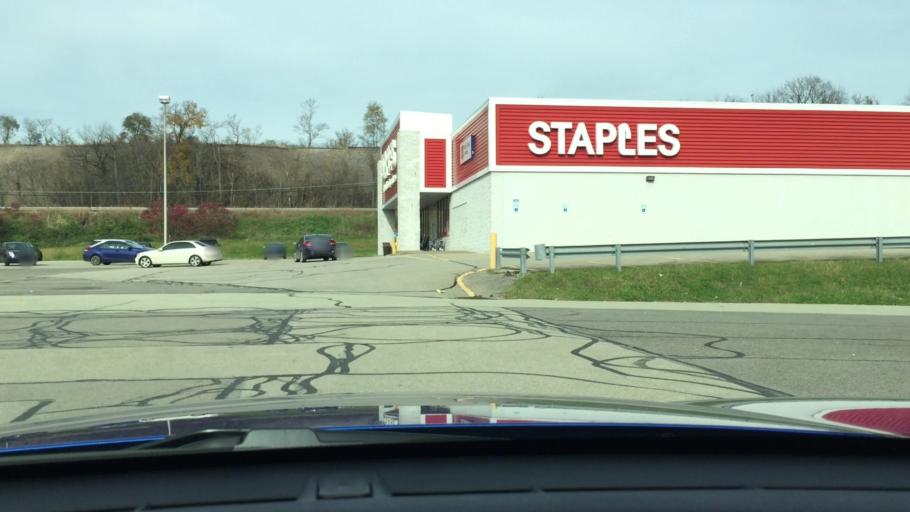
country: US
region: Pennsylvania
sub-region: Westmoreland County
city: Lynnwood-Pricedale
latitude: 40.1392
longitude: -79.8390
